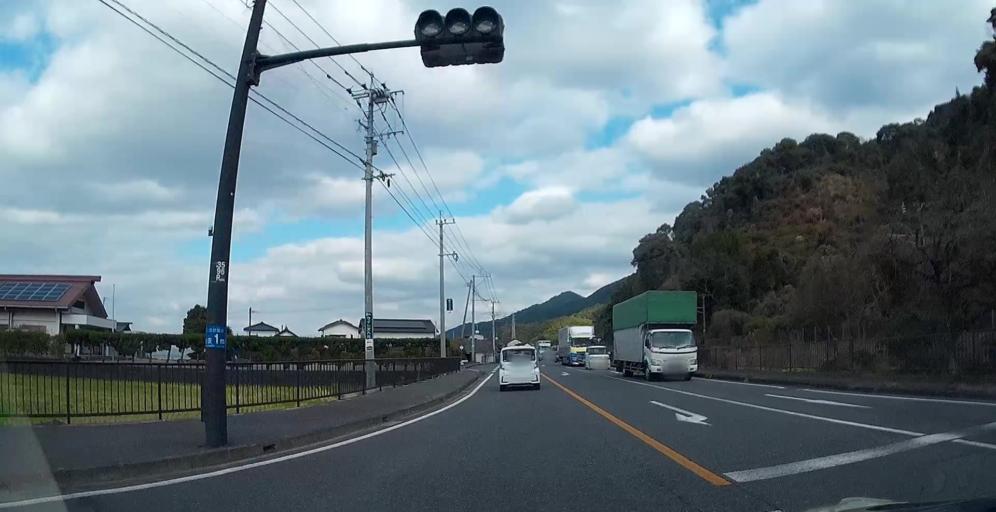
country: JP
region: Kumamoto
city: Yatsushiro
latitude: 32.4487
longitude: 130.5896
